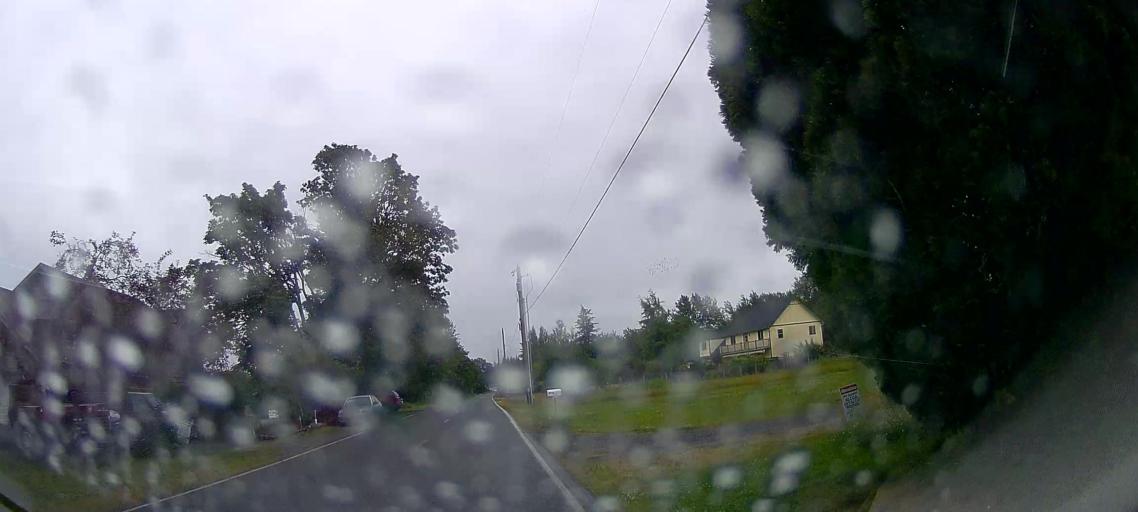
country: US
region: Washington
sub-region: Whatcom County
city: Marietta
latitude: 48.8052
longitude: -122.5717
